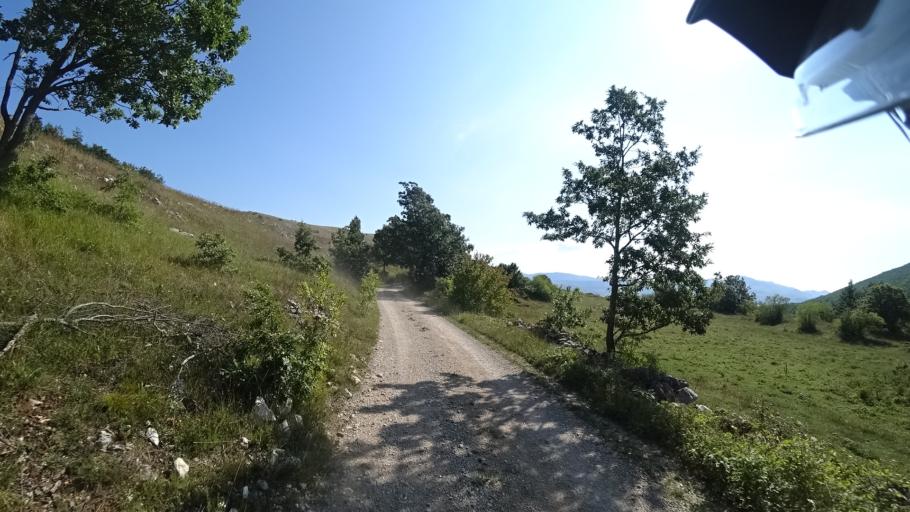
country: HR
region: Zadarska
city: Gracac
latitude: 44.3033
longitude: 16.0073
